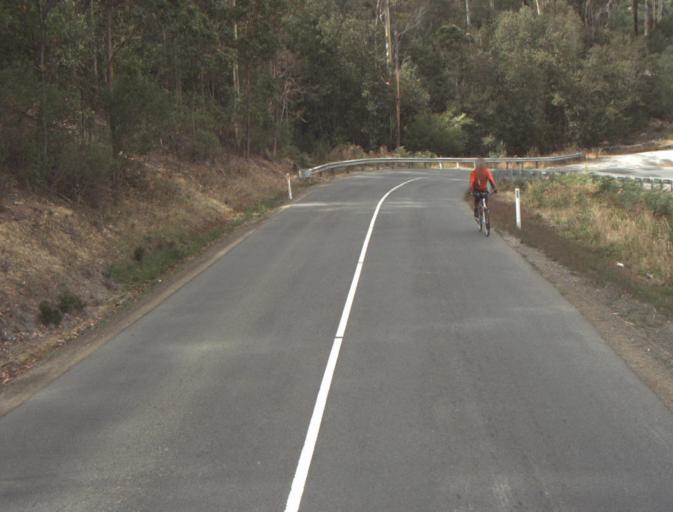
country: AU
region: Tasmania
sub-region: Launceston
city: Mayfield
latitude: -41.2238
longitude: 147.2083
